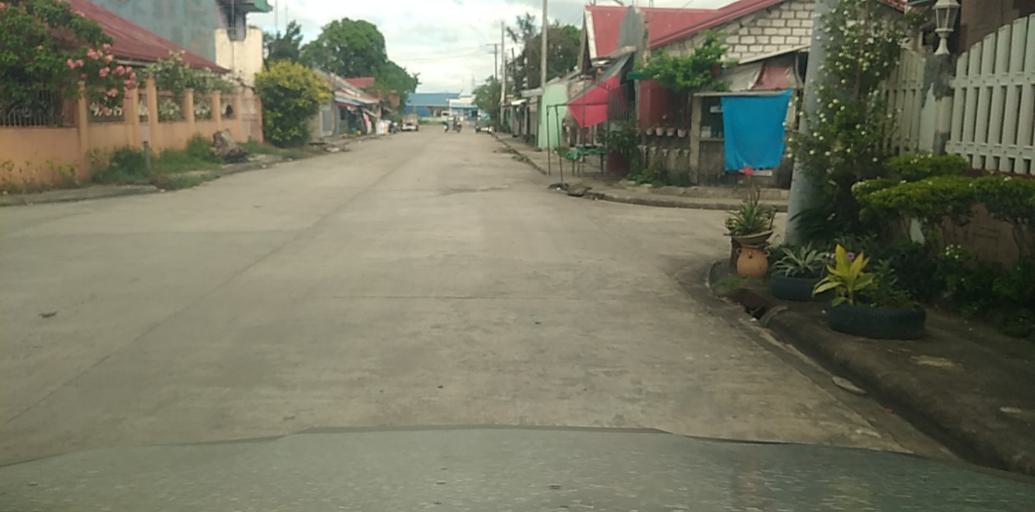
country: PH
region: Central Luzon
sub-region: Province of Pampanga
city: Pandacaqui
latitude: 15.1764
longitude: 120.6673
